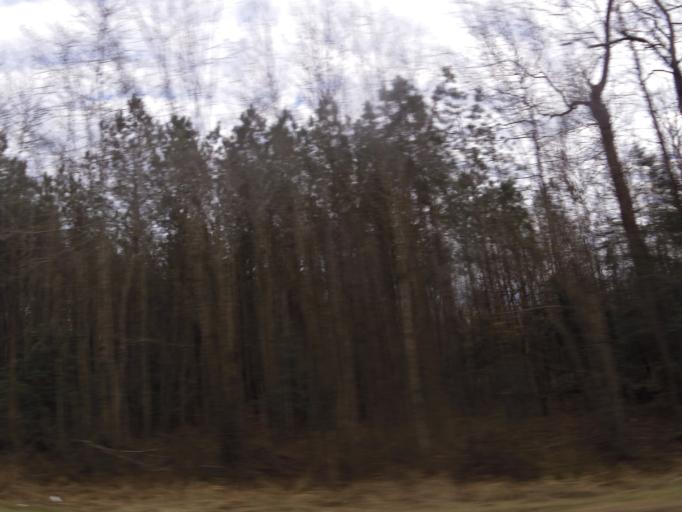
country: US
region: North Carolina
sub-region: Hertford County
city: Winton
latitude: 36.5188
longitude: -76.9841
